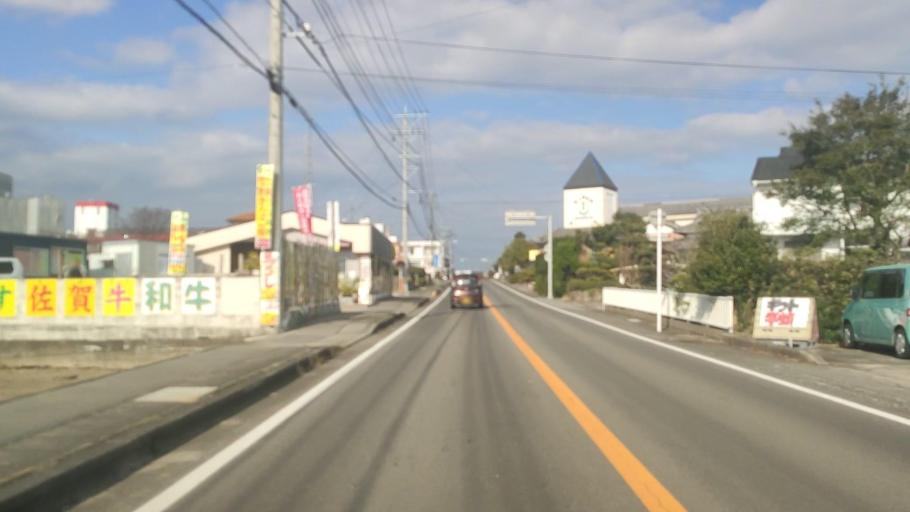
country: JP
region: Nagasaki
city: Shimabara
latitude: 32.6926
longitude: 130.3534
